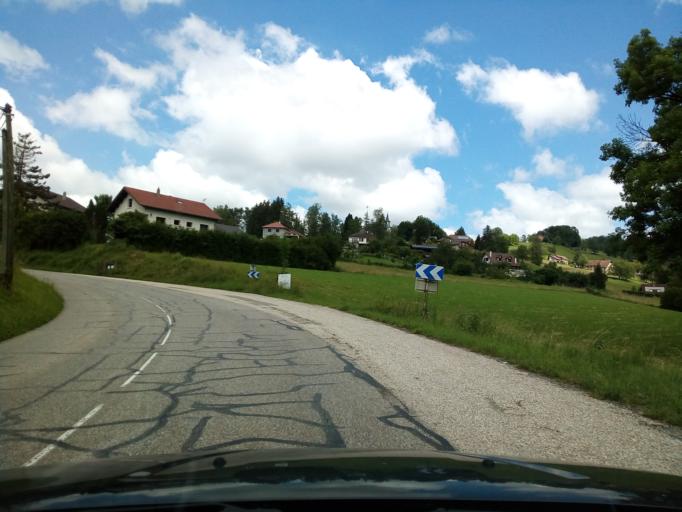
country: FR
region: Rhone-Alpes
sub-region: Departement de la Savoie
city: Les Echelles
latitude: 45.4469
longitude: 5.7535
